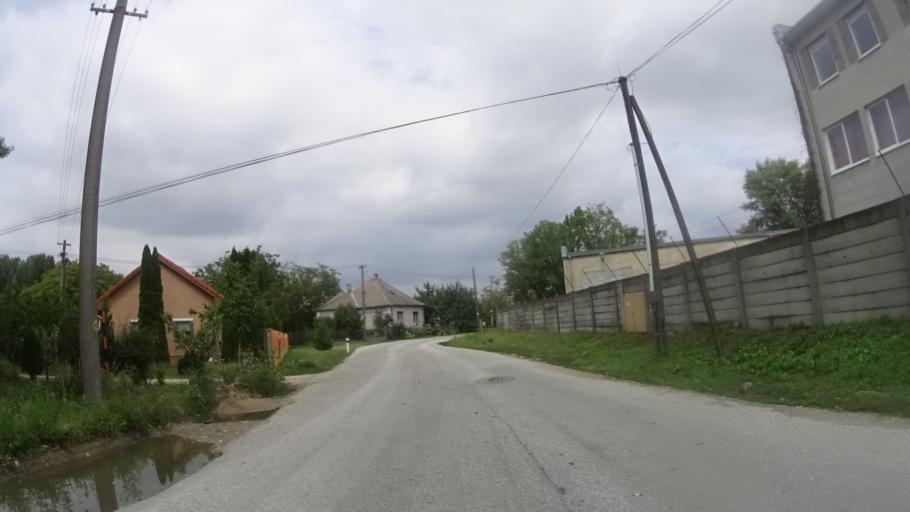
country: HU
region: Gyor-Moson-Sopron
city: Bony
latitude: 47.7473
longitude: 17.8777
